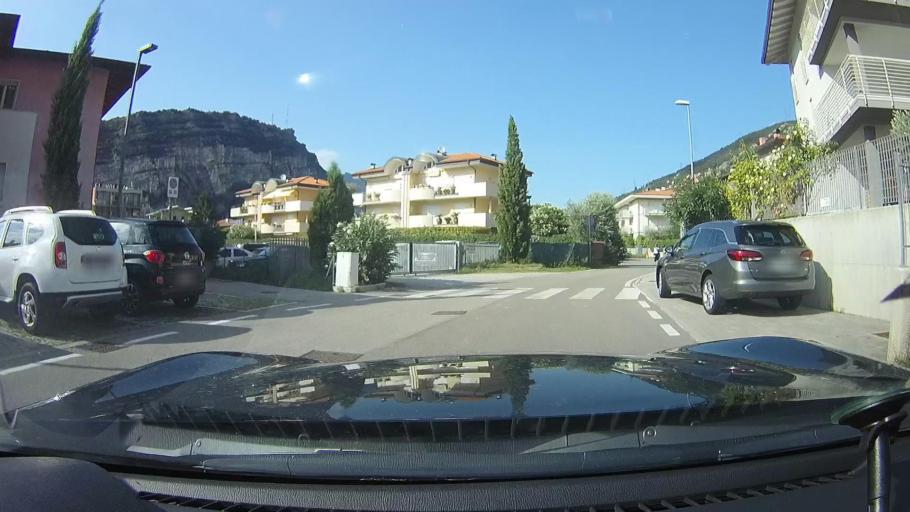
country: IT
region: Trentino-Alto Adige
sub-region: Provincia di Trento
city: Torbole sul Garda
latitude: 45.8739
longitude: 10.8784
